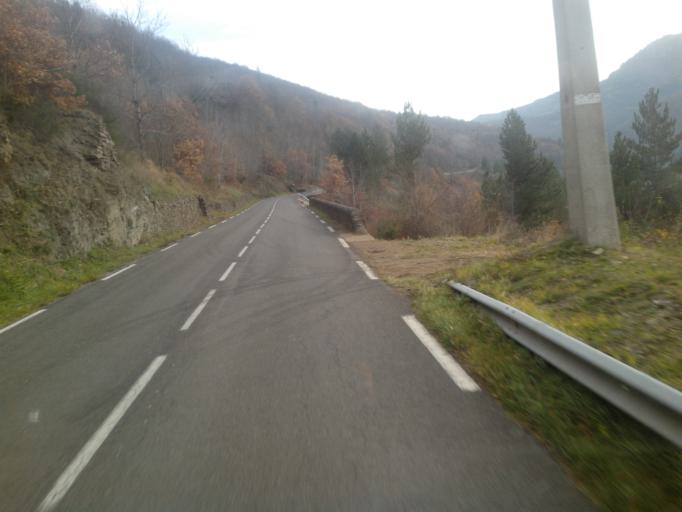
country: FR
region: Languedoc-Roussillon
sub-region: Departement de la Lozere
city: Florac
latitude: 44.3750
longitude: 3.5550
